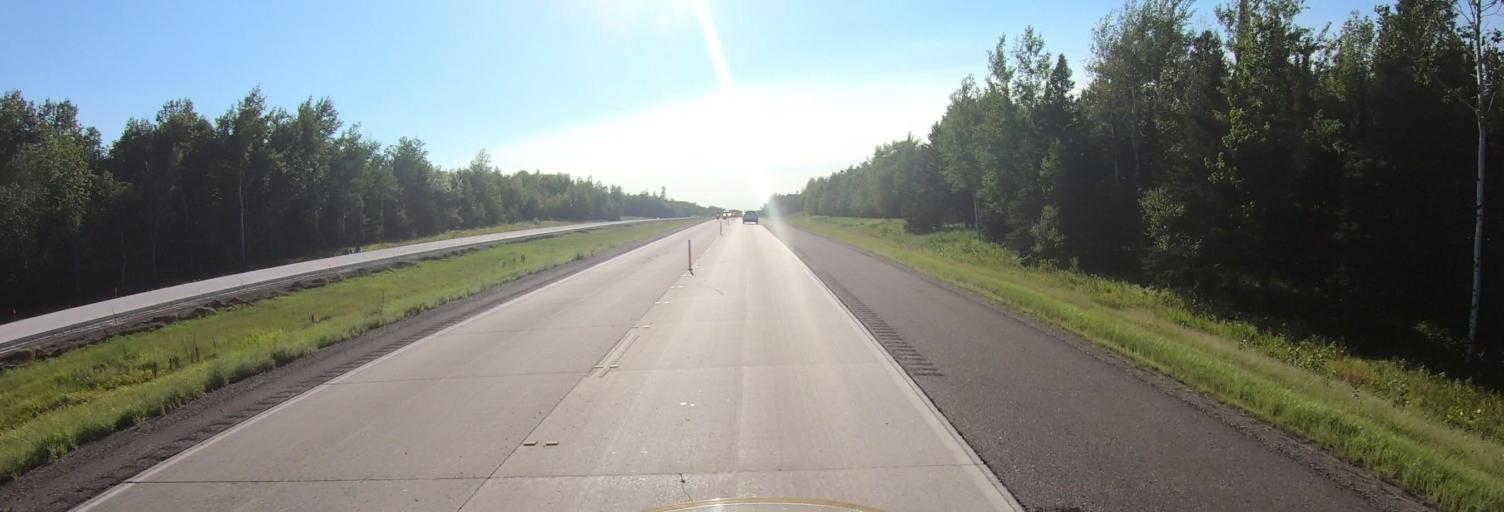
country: US
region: Minnesota
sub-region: Saint Louis County
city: Hermantown
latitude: 46.8530
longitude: -92.2946
